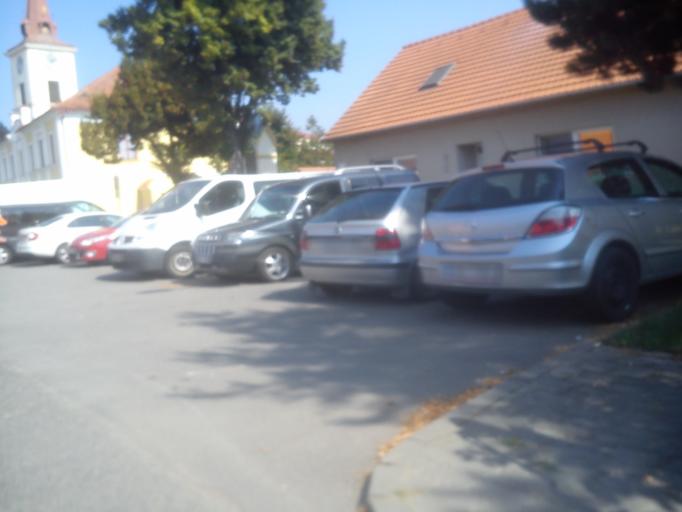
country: CZ
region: South Moravian
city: Sokolnice
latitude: 49.1038
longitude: 16.7558
